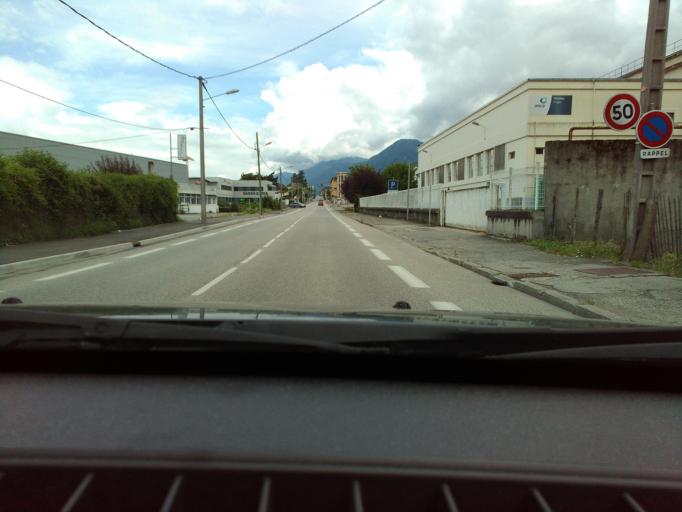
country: FR
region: Rhone-Alpes
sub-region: Departement de l'Isere
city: Froges
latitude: 45.2692
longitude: 5.9201
